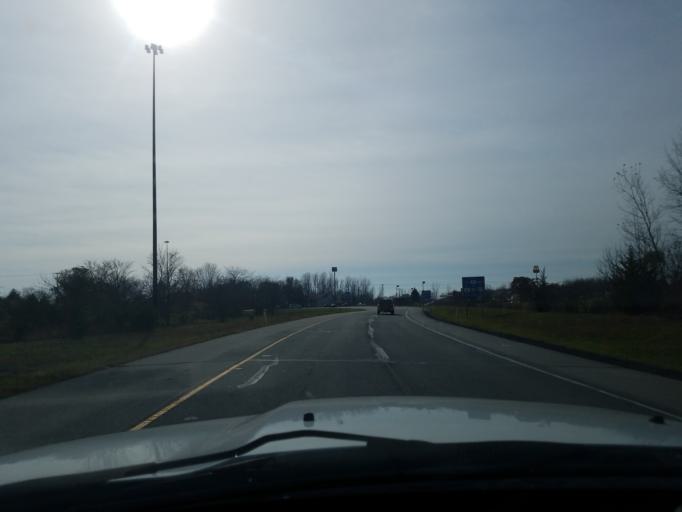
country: US
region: Indiana
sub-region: Delaware County
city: Daleville
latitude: 40.1160
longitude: -85.5695
